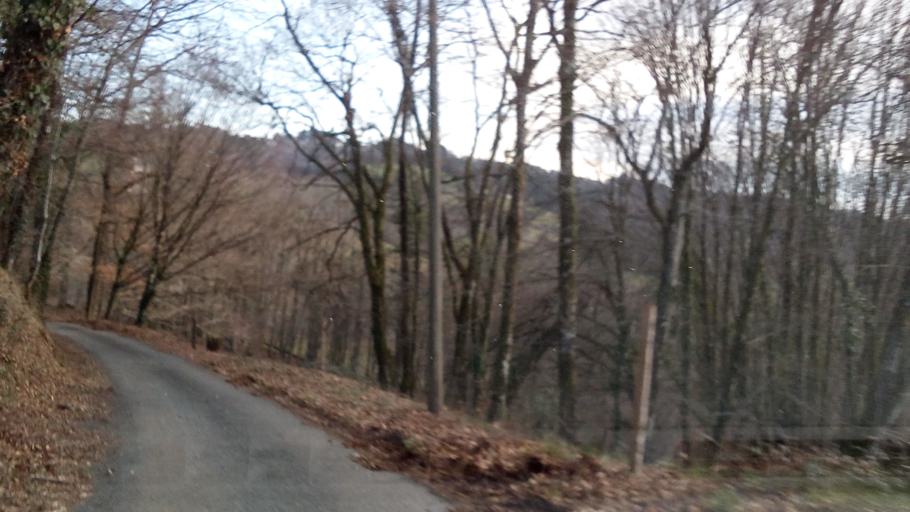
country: FR
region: Limousin
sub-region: Departement de la Correze
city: Naves
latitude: 45.3099
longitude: 1.7914
